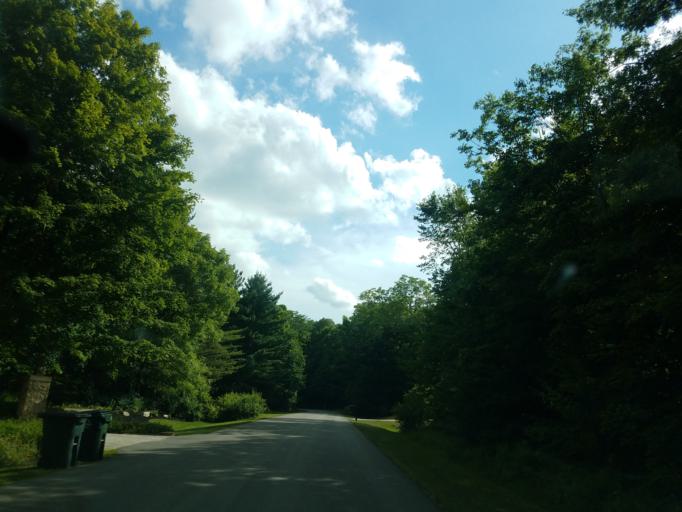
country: US
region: Ohio
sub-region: Delaware County
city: Powell
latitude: 40.1939
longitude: -83.0669
